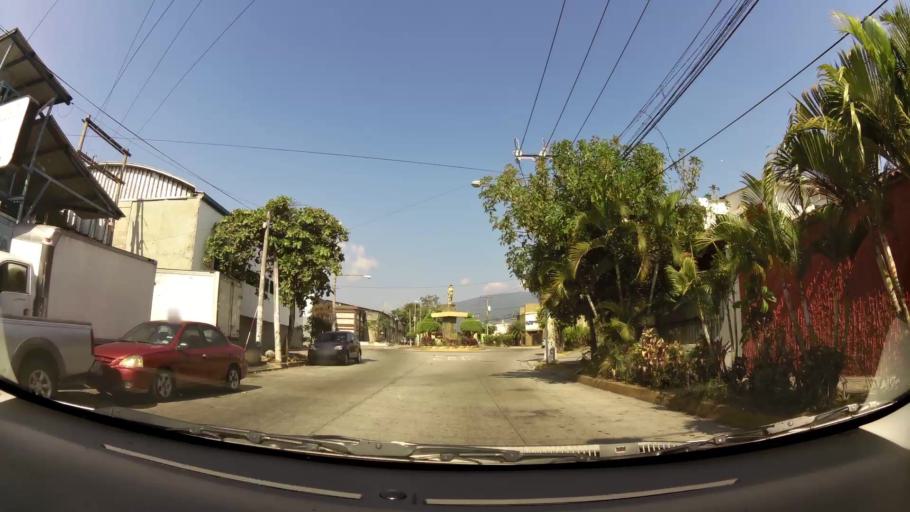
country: SV
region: La Libertad
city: Antiguo Cuscatlan
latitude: 13.6742
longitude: -89.2430
